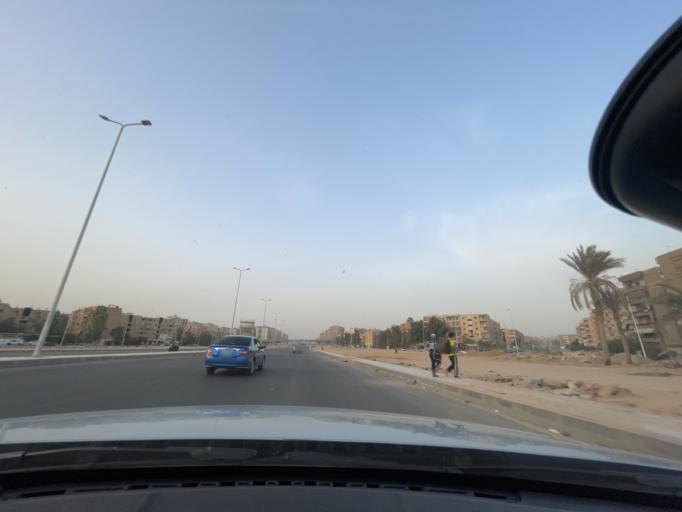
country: EG
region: Muhafazat al Qahirah
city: Cairo
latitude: 30.0434
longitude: 31.3621
